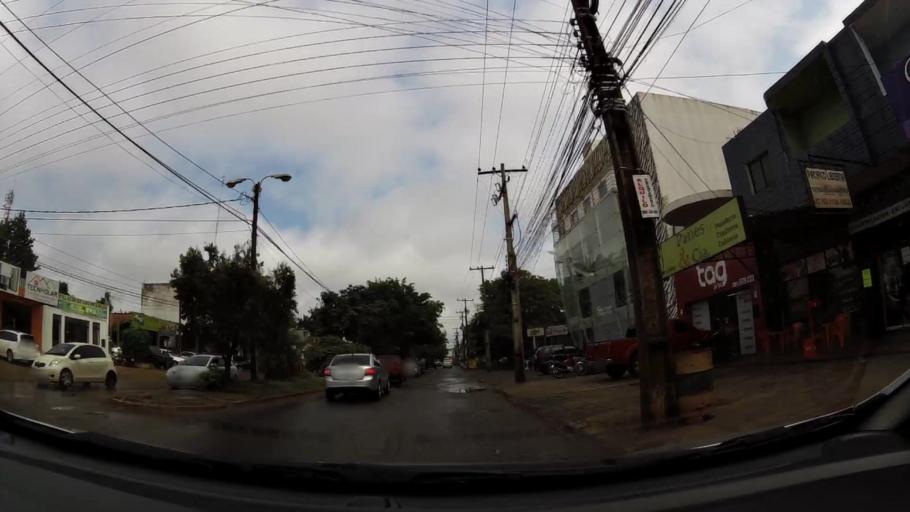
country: PY
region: Alto Parana
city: Presidente Franco
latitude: -25.5132
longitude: -54.6515
